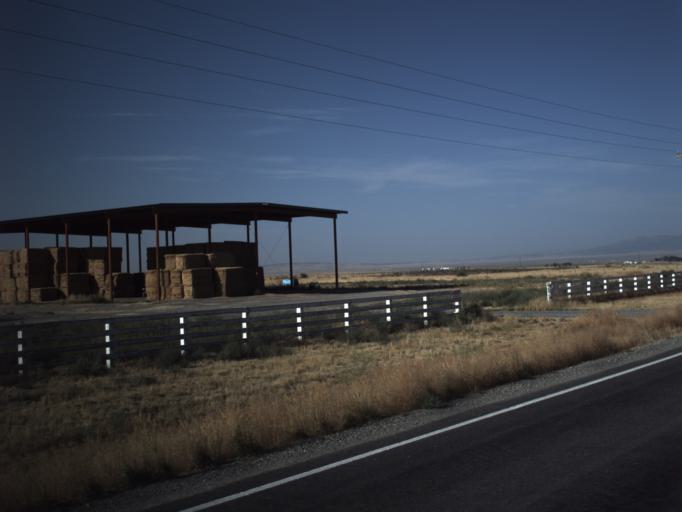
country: US
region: Idaho
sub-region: Oneida County
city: Malad City
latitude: 41.9673
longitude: -112.8051
